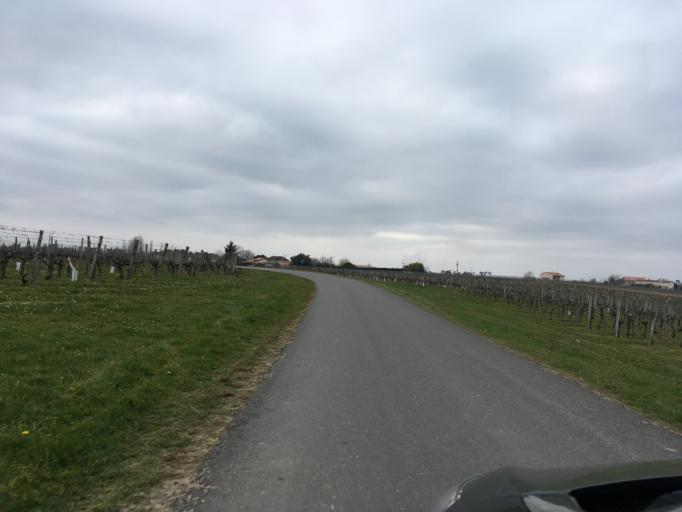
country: FR
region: Aquitaine
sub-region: Departement de la Gironde
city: Saint-Ciers-sur-Gironde
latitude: 45.3091
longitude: -0.5925
